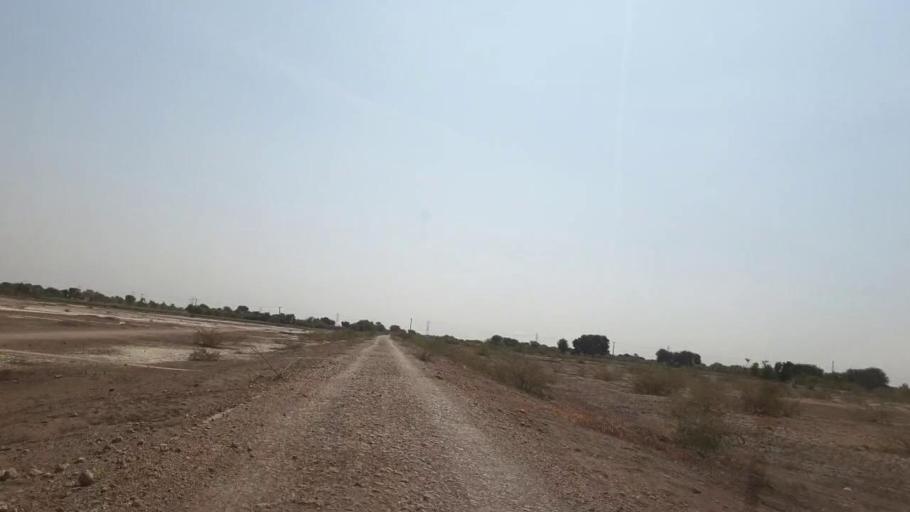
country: PK
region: Sindh
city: Nabisar
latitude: 25.0713
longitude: 69.5527
